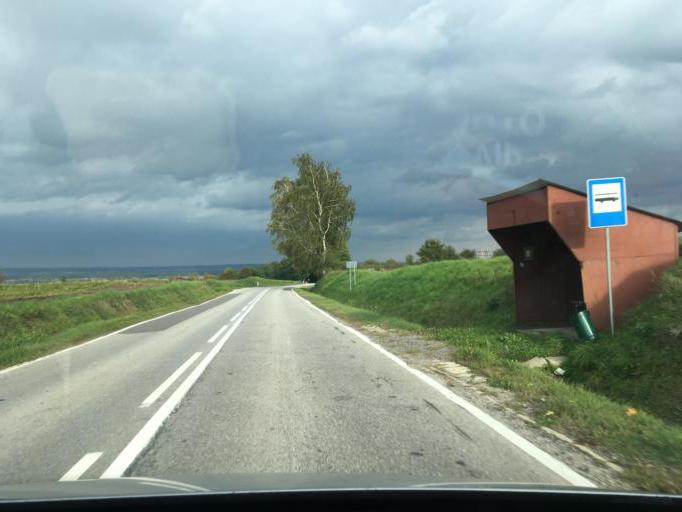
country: PL
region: Swietokrzyskie
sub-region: Powiat pinczowski
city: Michalow
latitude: 50.4730
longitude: 20.4296
